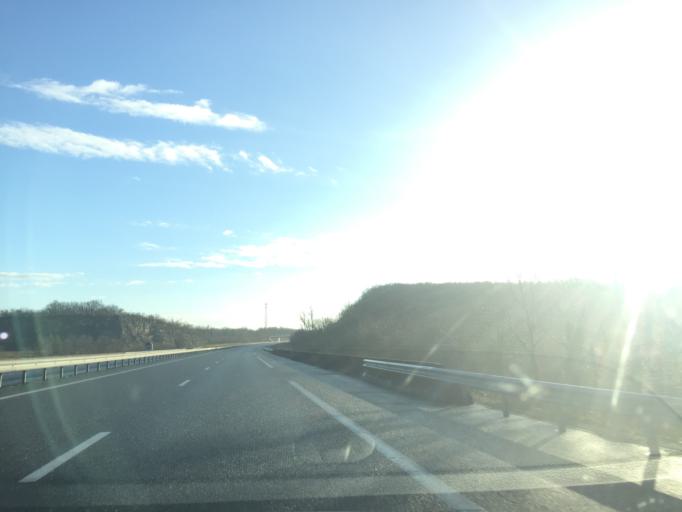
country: FR
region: Aquitaine
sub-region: Departement de la Dordogne
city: Thenon
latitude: 45.1634
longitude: 1.0455
